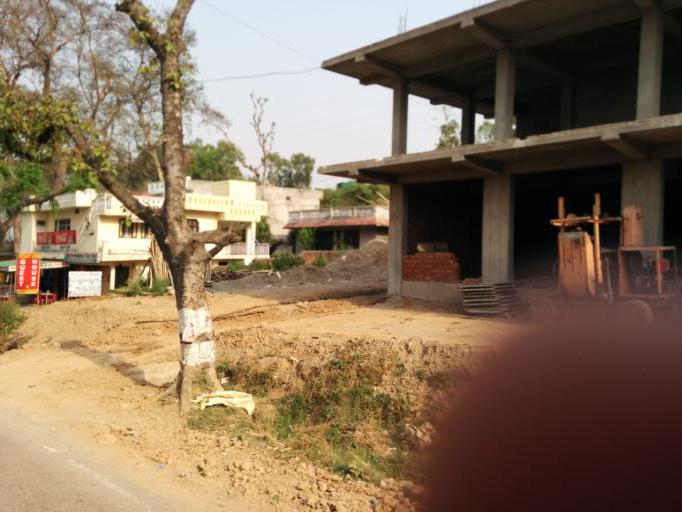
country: IN
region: Himachal Pradesh
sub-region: Kangra
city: Kotla
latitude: 32.2985
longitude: 75.9038
